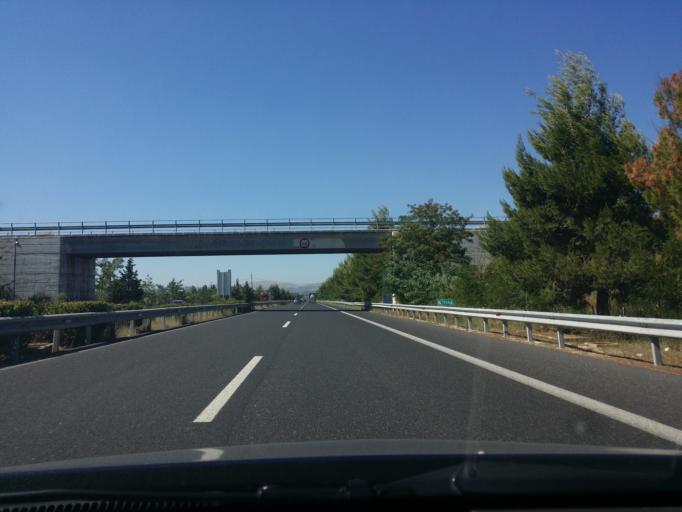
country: GR
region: Peloponnese
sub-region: Nomos Arkadias
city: Tripoli
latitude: 37.5357
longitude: 22.4134
